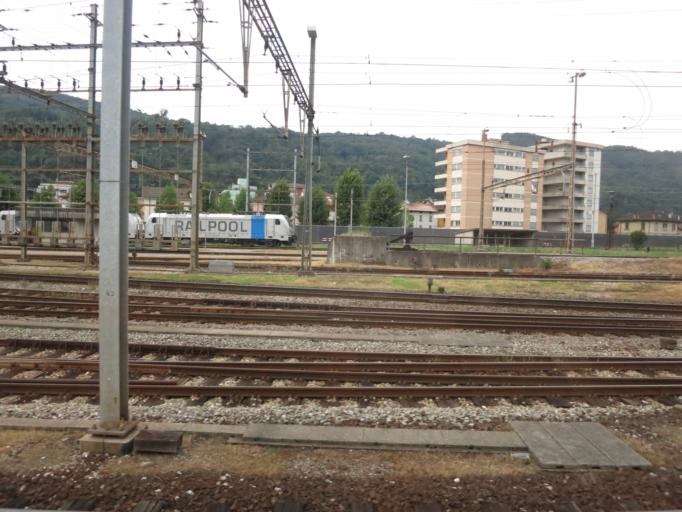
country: CH
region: Ticino
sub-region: Mendrisio District
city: Chiasso
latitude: 45.8349
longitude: 9.0247
